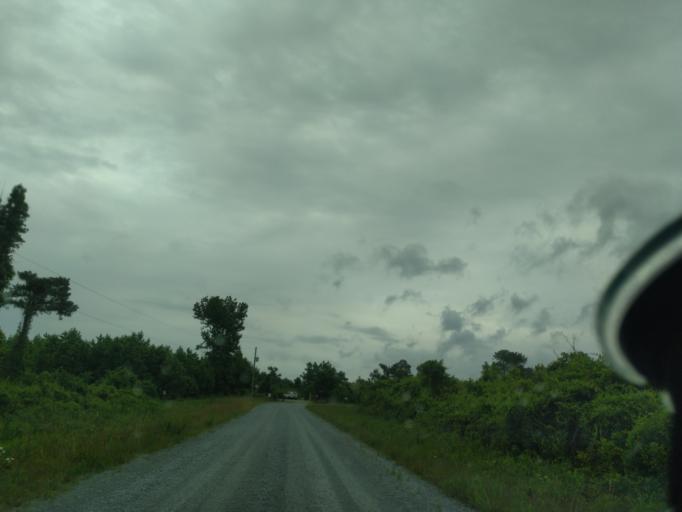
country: US
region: North Carolina
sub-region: Beaufort County
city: Belhaven
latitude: 35.7325
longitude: -76.4437
